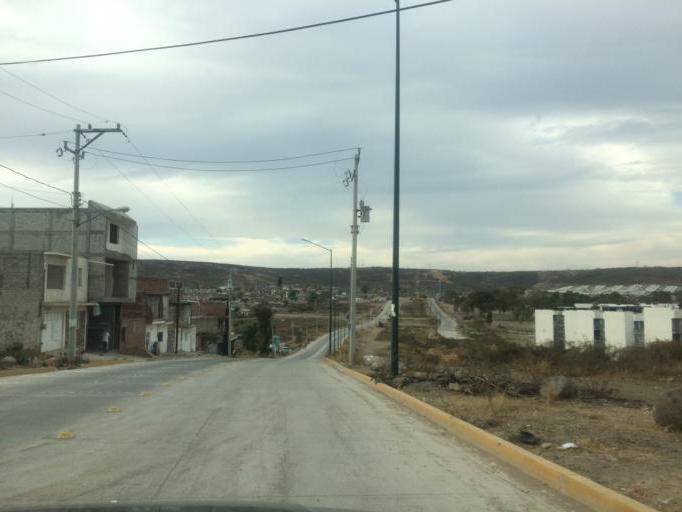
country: MX
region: Guanajuato
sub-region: Leon
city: Rizos de la Joya (Rizos del Saucillo)
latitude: 21.1436
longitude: -101.7541
